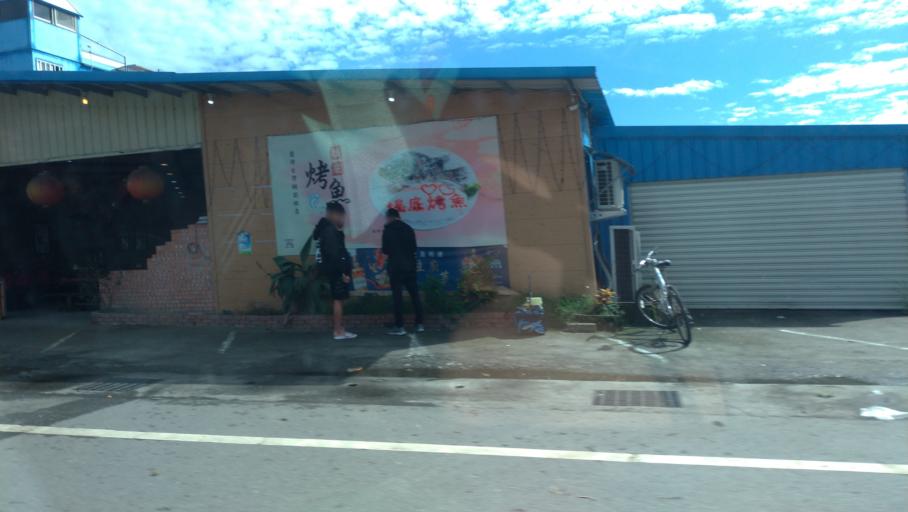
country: TW
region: Taiwan
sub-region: Yilan
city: Yilan
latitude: 24.8178
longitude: 121.7960
